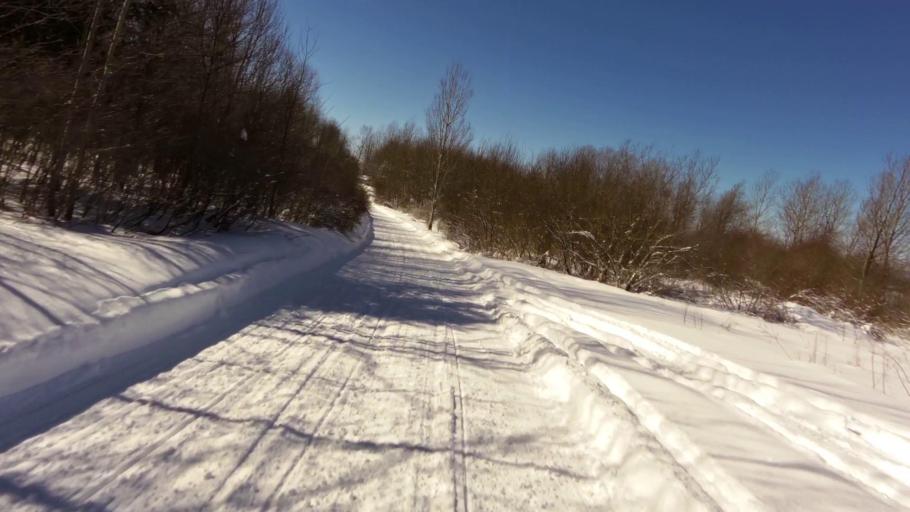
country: US
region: New York
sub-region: Chautauqua County
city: Mayville
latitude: 42.2360
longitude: -79.3908
